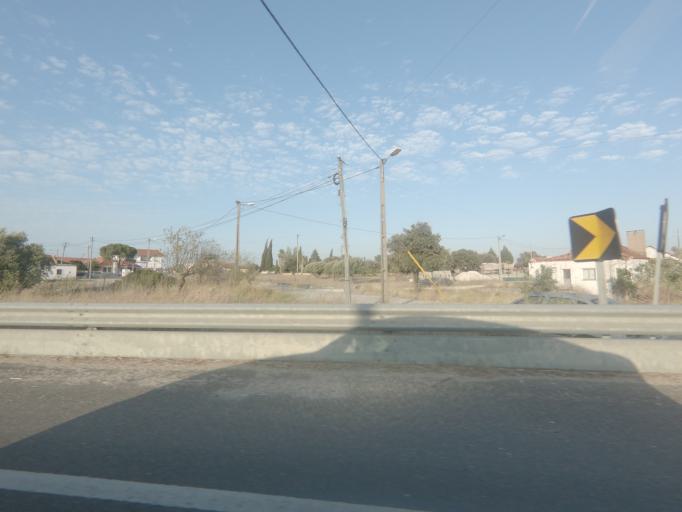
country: PT
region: Santarem
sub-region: Alcanena
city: Alcanena
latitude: 39.4824
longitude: -8.6329
